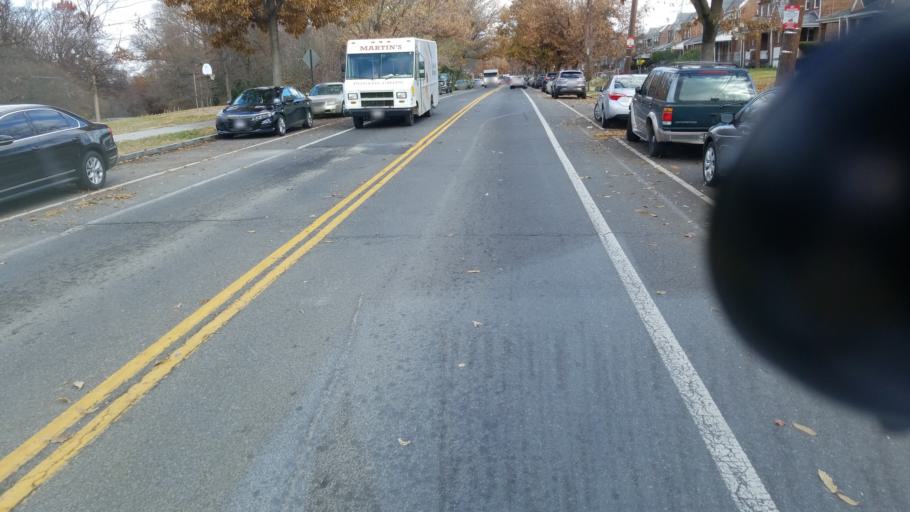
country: US
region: Maryland
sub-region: Prince George's County
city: Silver Hill
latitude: 38.8672
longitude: -76.9496
